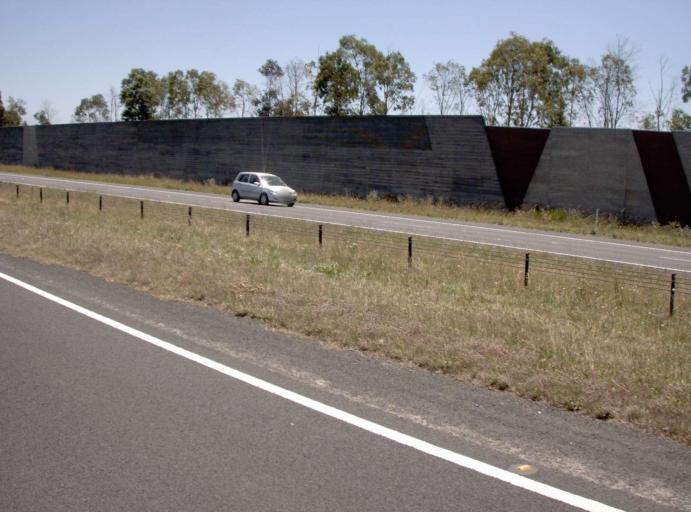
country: AU
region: Victoria
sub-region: Cardinia
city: Officer South
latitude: -38.0853
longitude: 145.4500
